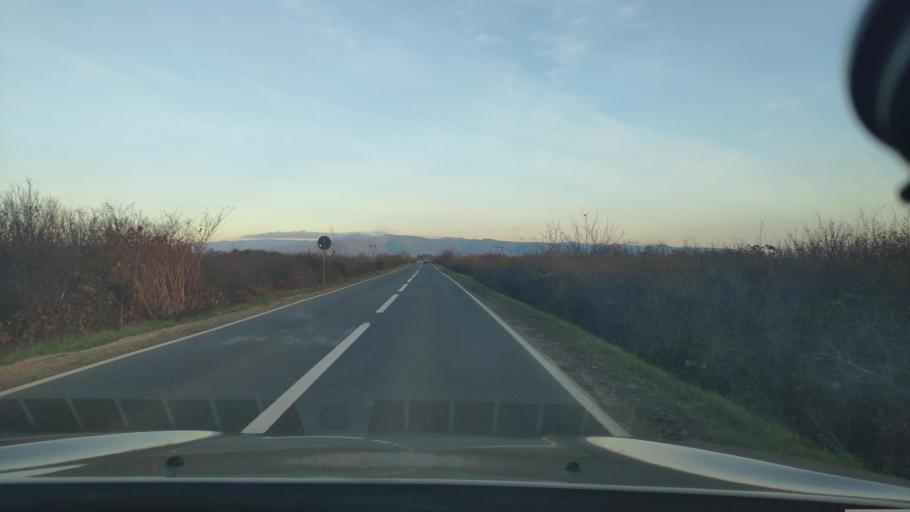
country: RO
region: Satu Mare
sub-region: Comuna Mediesu Aurit
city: Mediesu Aurit
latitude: 47.7672
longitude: 23.1614
